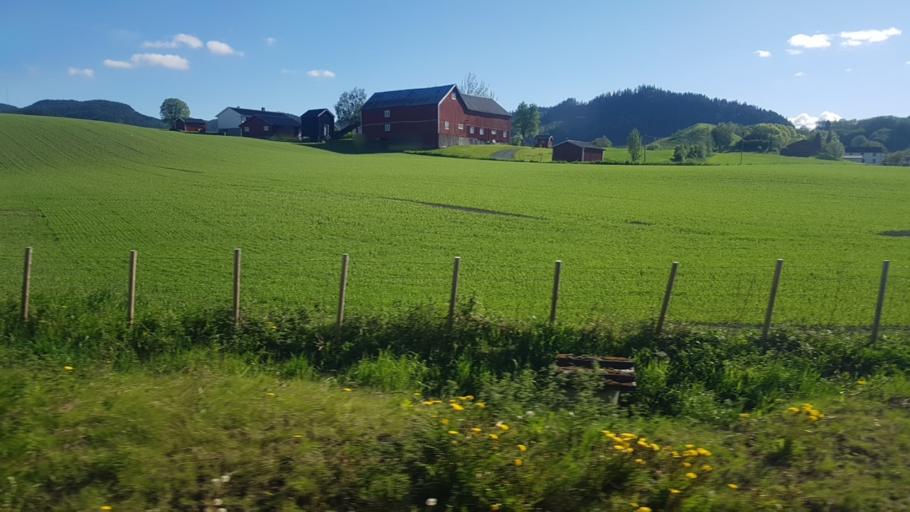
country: NO
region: Sor-Trondelag
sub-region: Melhus
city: Lundamo
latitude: 63.2018
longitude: 10.3059
